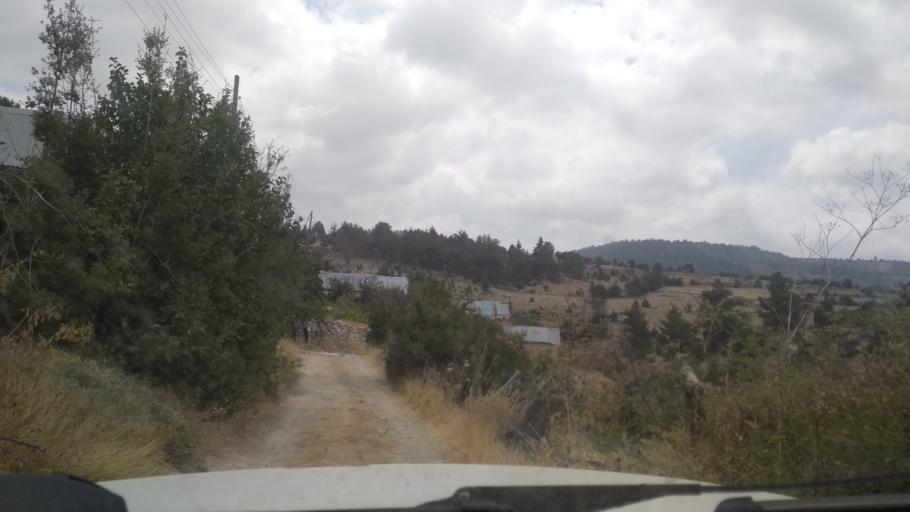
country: TR
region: Mersin
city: Sarikavak
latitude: 36.5993
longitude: 33.7273
